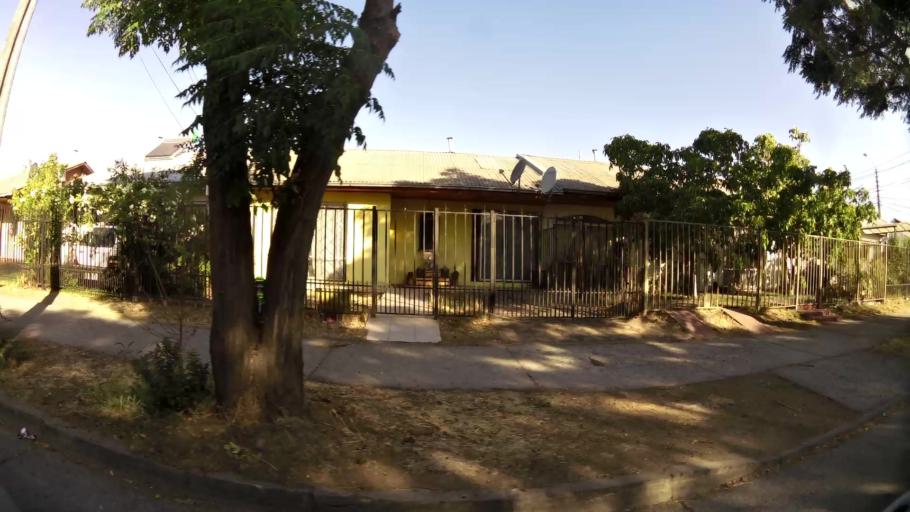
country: CL
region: Maule
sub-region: Provincia de Talca
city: Talca
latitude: -35.4412
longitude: -71.6901
